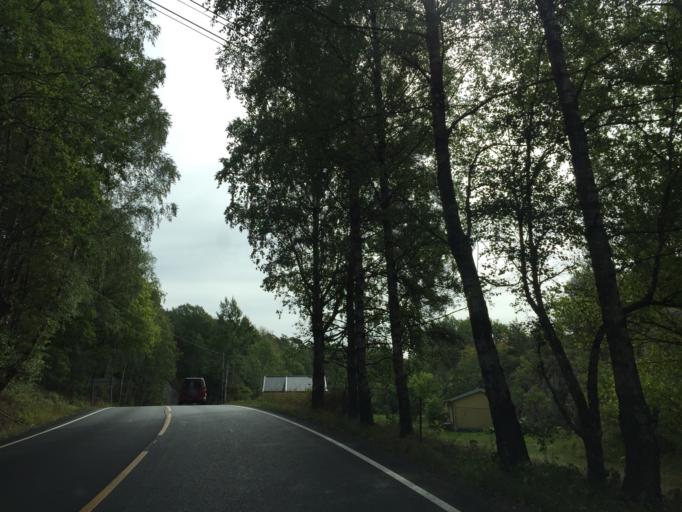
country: NO
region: Ostfold
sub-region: Fredrikstad
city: Fredrikstad
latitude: 59.1026
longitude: 10.9042
